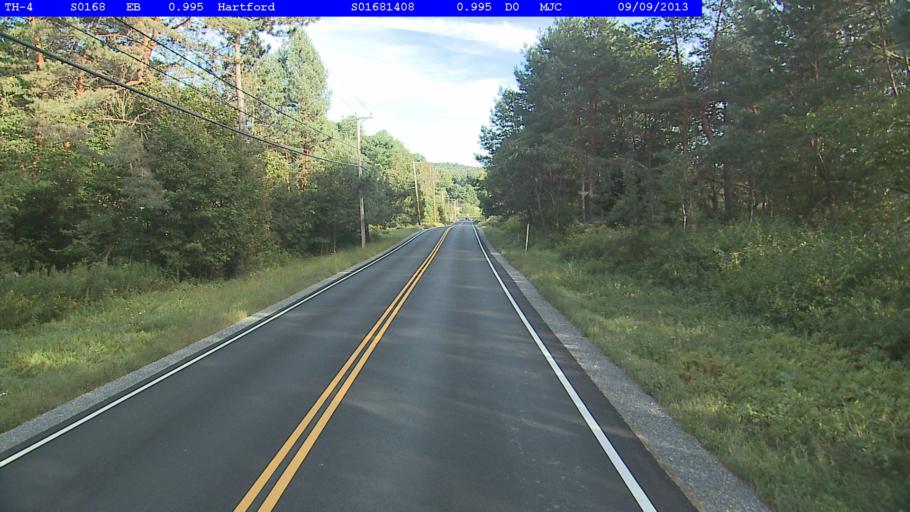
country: US
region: Vermont
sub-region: Windsor County
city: White River Junction
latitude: 43.6477
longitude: -72.4036
